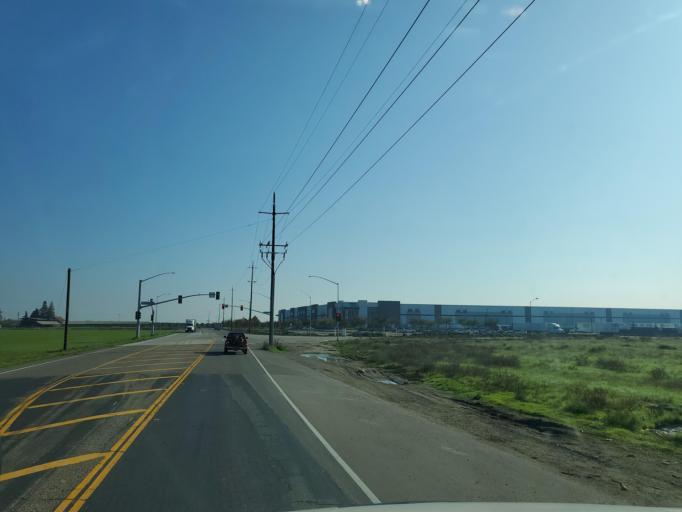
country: US
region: California
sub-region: San Joaquin County
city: French Camp
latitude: 37.8556
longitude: -121.2613
